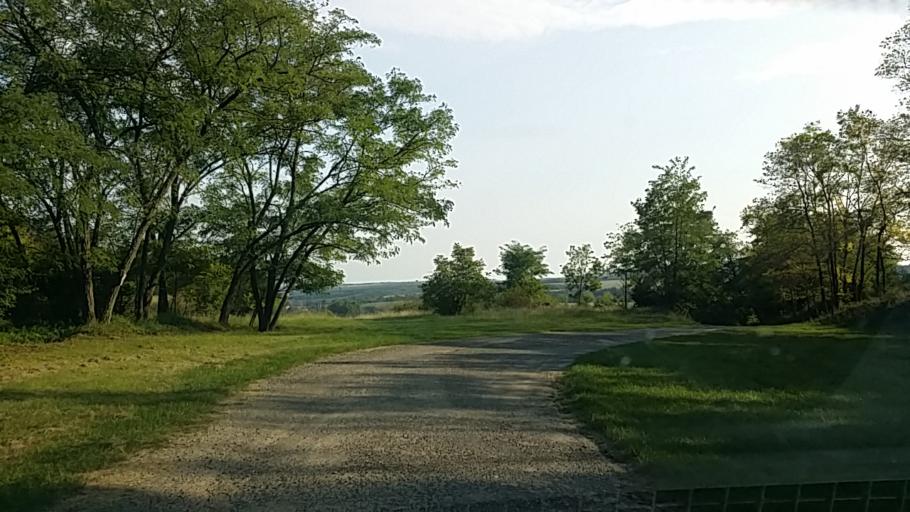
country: HU
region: Nograd
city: Bujak
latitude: 47.8707
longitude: 19.5008
